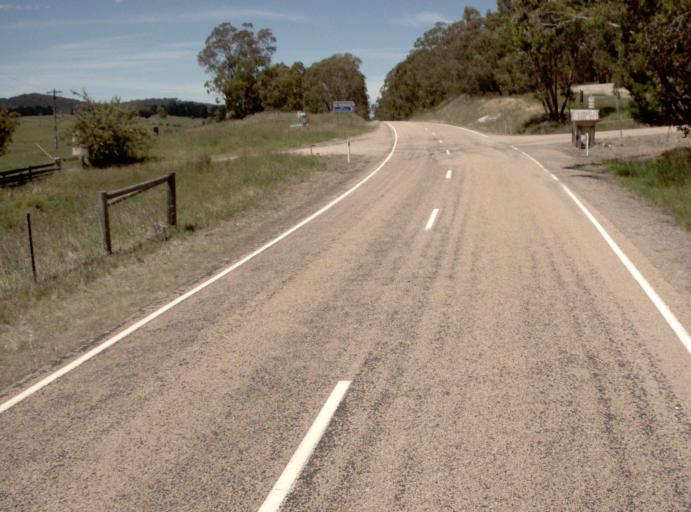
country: AU
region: Victoria
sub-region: East Gippsland
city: Lakes Entrance
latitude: -37.1862
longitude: 148.2689
